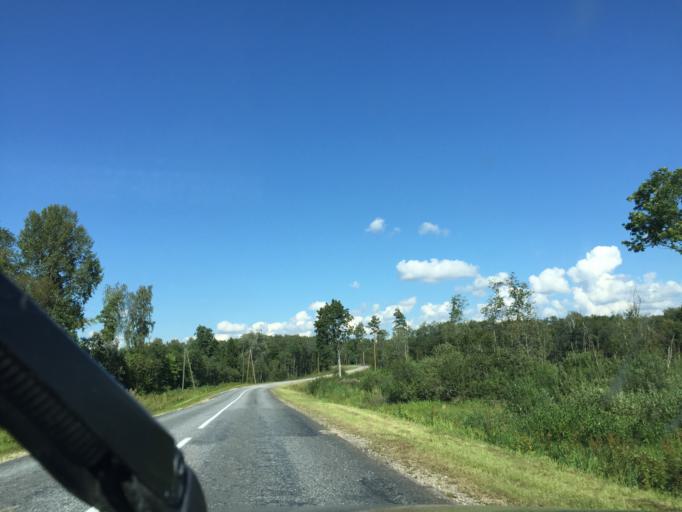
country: LV
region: Limbazu Rajons
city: Limbazi
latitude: 57.4383
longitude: 24.7187
